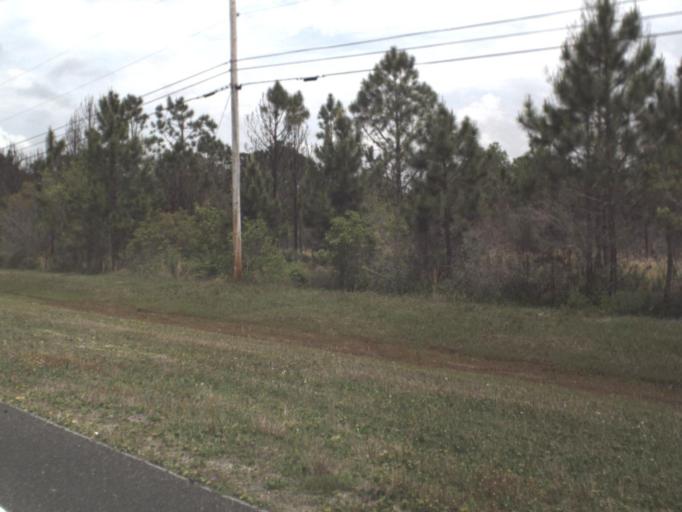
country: US
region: Florida
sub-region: Santa Rosa County
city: Tiger Point
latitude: 30.4873
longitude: -87.0798
